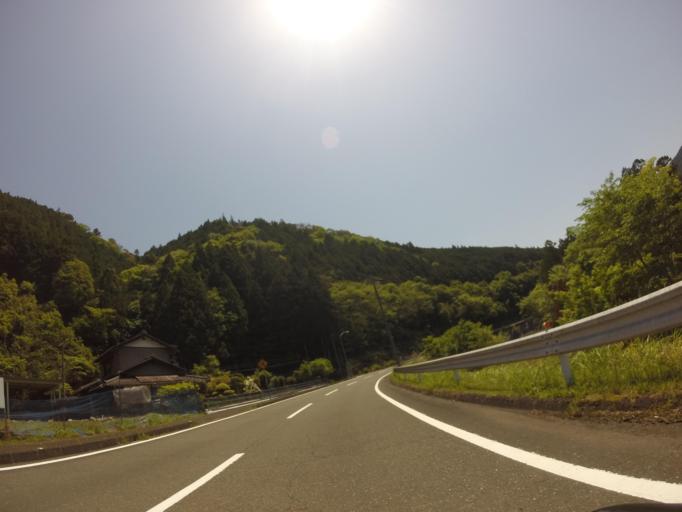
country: JP
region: Shizuoka
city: Shizuoka-shi
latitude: 35.0883
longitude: 138.2450
